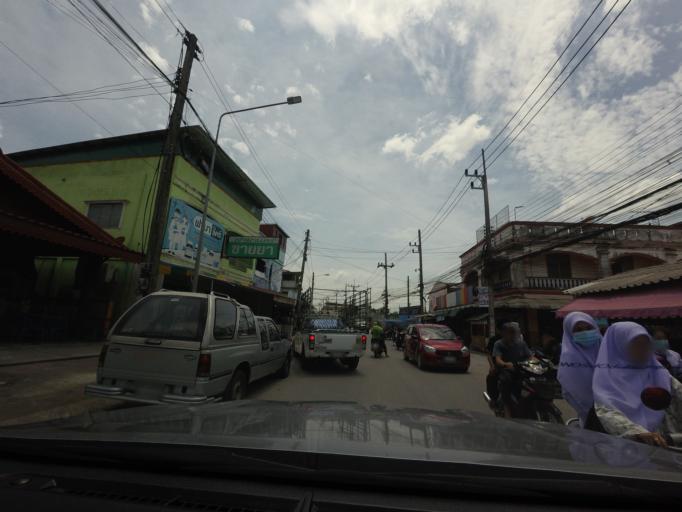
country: TH
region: Yala
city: Yala
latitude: 6.5402
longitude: 101.2932
